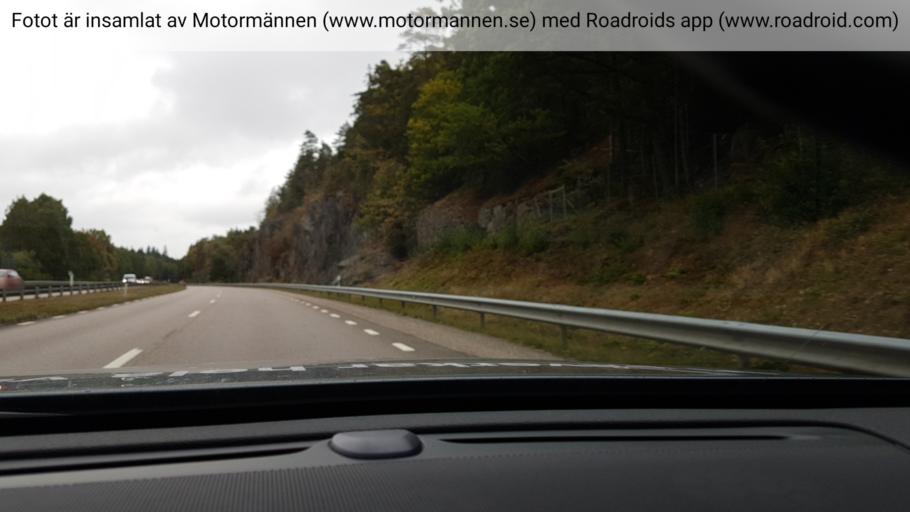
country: SE
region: Vaestra Goetaland
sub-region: Alingsas Kommun
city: Ingared
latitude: 57.8306
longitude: 12.4334
